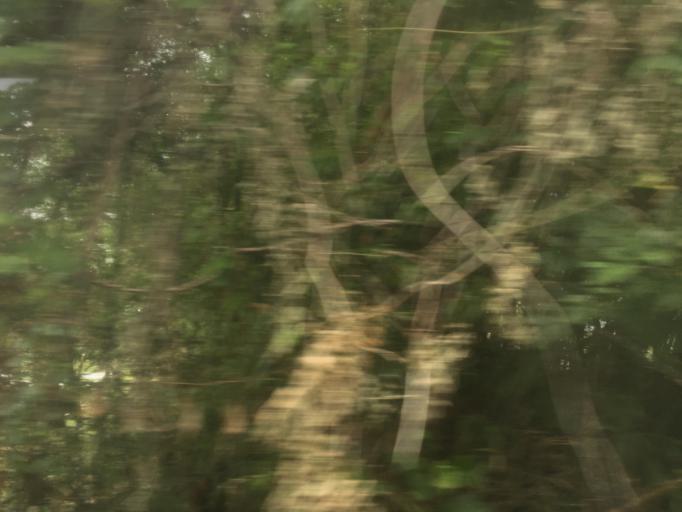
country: JP
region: Gunma
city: Takasaki
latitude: 36.2871
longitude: 139.0245
